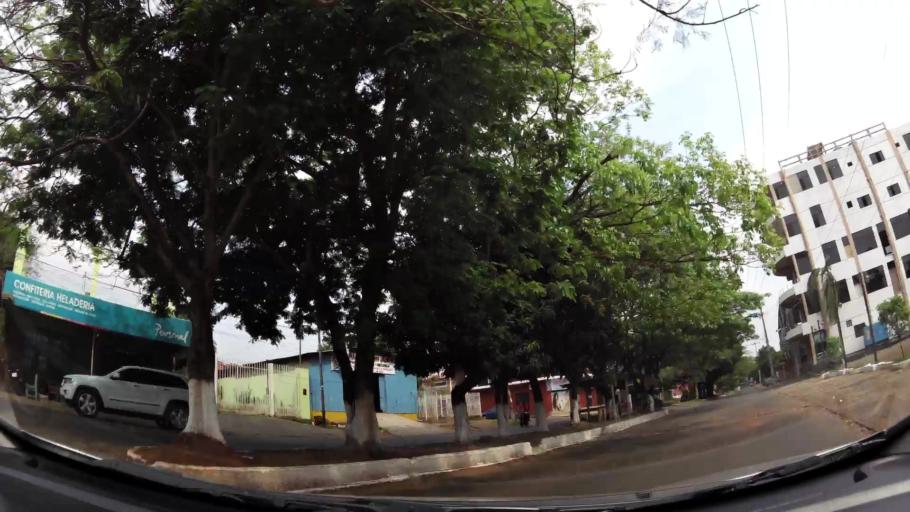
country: PY
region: Alto Parana
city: Presidente Franco
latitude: -25.5357
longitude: -54.6066
